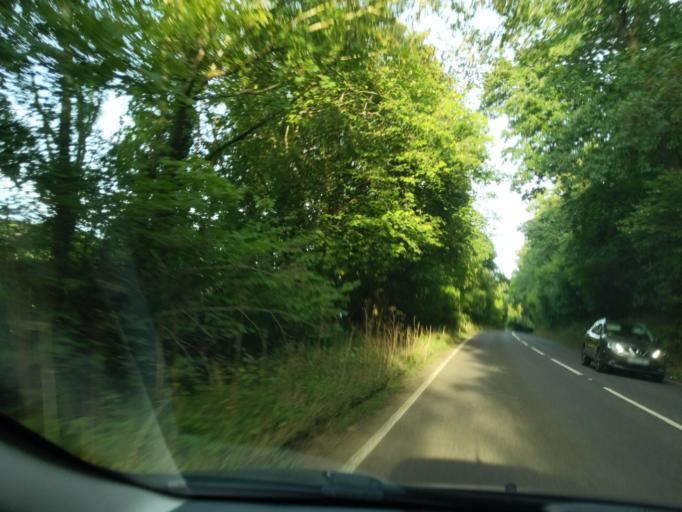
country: GB
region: England
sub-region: Cornwall
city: Saltash
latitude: 50.3712
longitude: -4.2820
